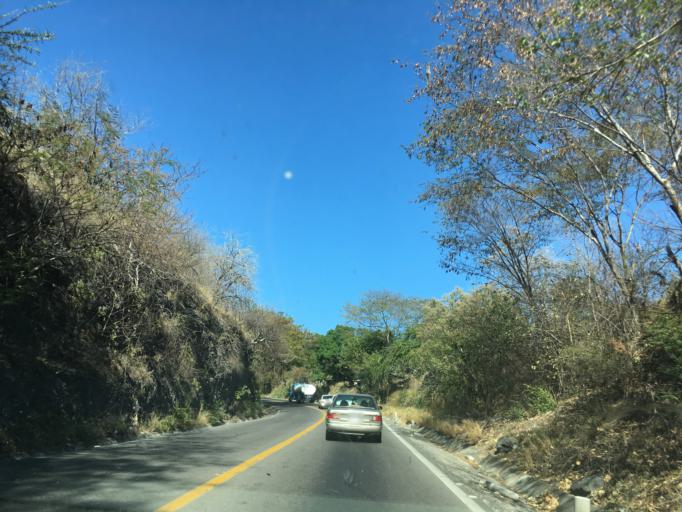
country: MX
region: Michoacan
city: Nueva Italia de Ruiz
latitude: 19.0851
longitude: -102.0596
